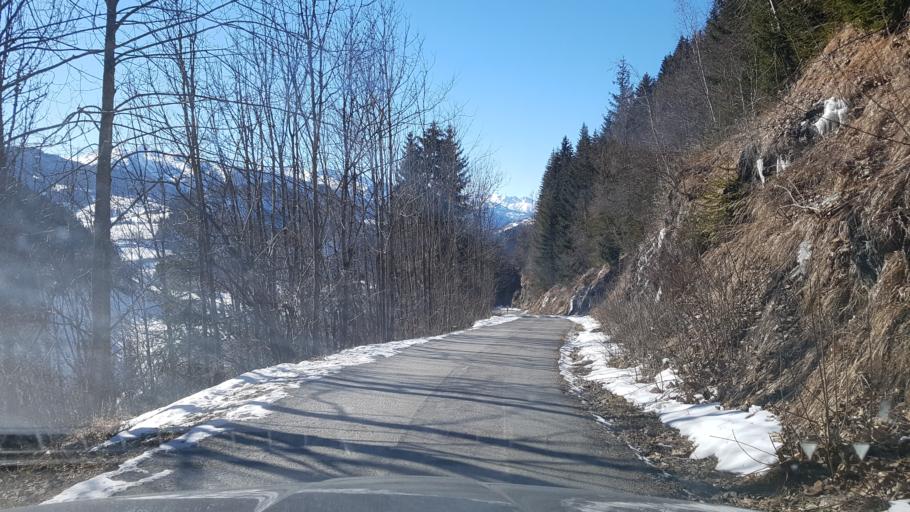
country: AT
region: Salzburg
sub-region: Politischer Bezirk Zell am See
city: Lend
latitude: 47.3159
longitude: 13.0483
